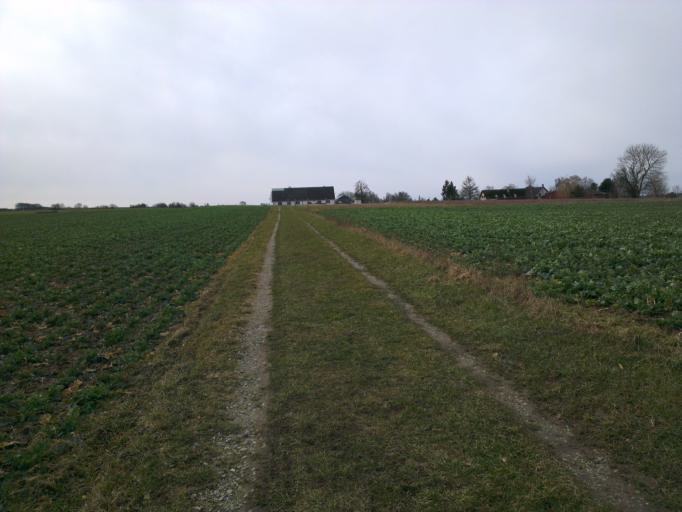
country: DK
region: Capital Region
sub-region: Frederikssund Kommune
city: Skibby
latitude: 55.7896
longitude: 11.8687
